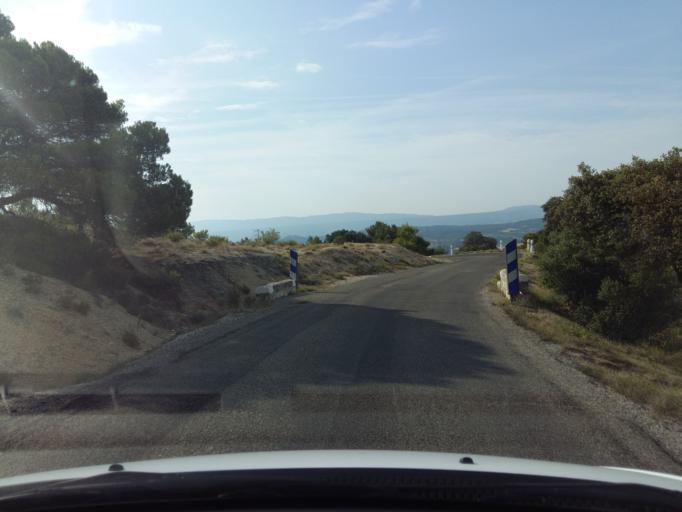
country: FR
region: Provence-Alpes-Cote d'Azur
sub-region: Departement du Vaucluse
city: Roussillon
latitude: 43.9462
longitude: 5.2545
